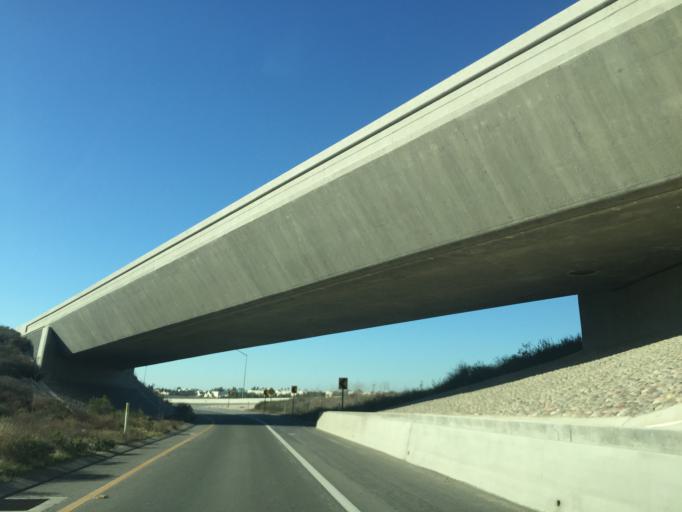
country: MX
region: Baja California
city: Tijuana
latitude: 32.5638
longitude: -116.9489
